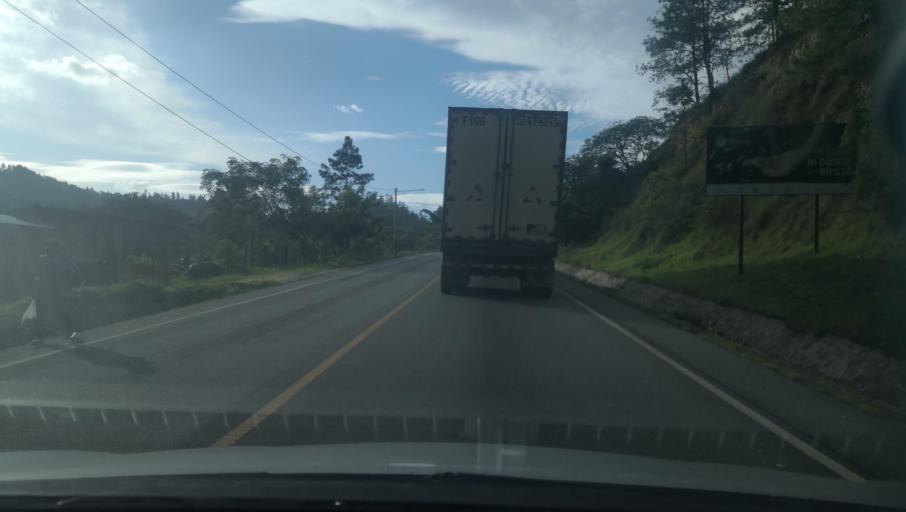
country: NI
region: Nueva Segovia
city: Mozonte
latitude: 13.7168
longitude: -86.5042
